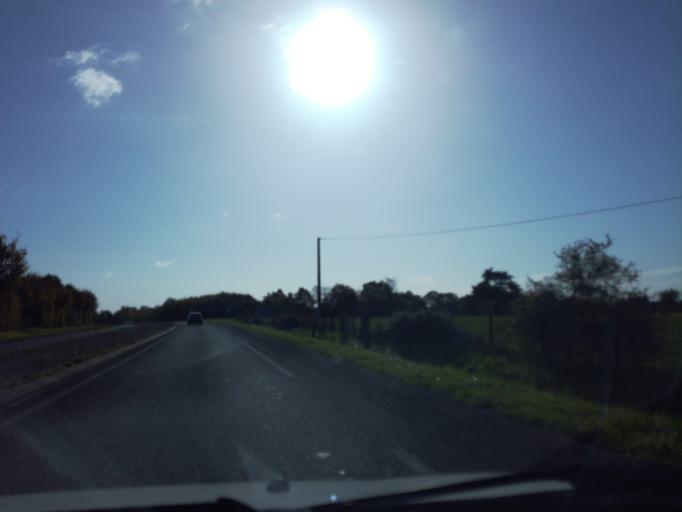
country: FR
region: Pays de la Loire
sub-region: Departement de la Loire-Atlantique
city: Soudan
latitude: 47.7774
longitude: -1.2422
